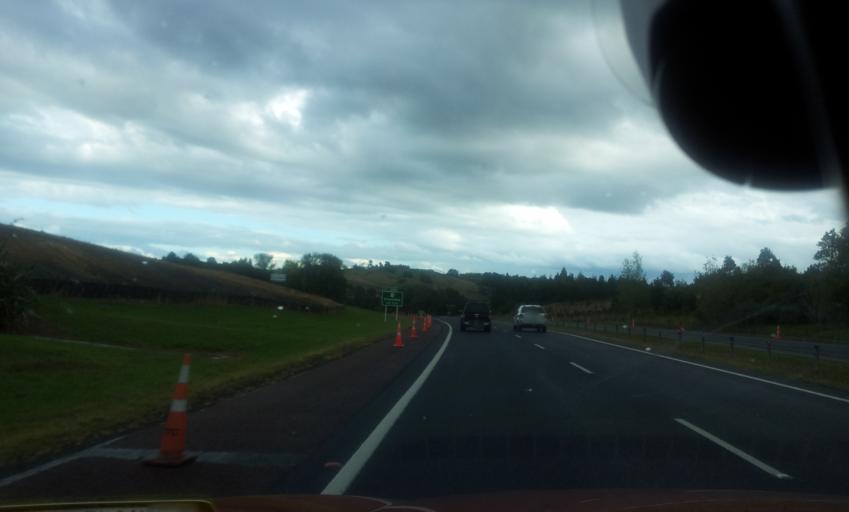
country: NZ
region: Auckland
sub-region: Auckland
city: Rothesay Bay
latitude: -36.6127
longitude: 174.6604
